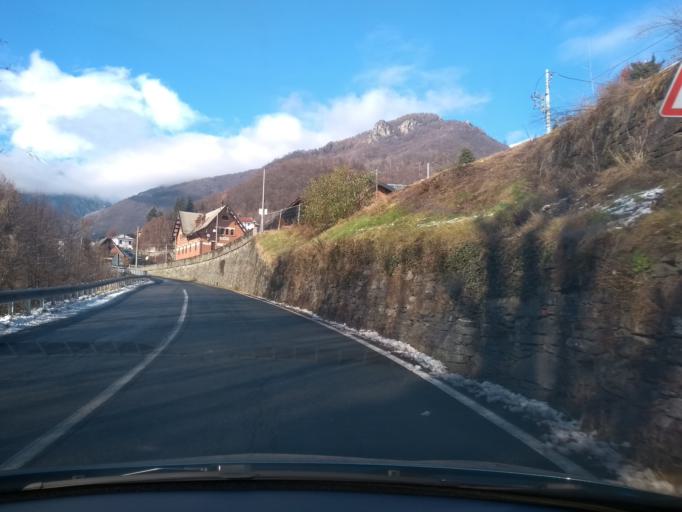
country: IT
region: Piedmont
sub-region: Provincia di Torino
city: Ceres
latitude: 45.3104
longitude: 7.3910
